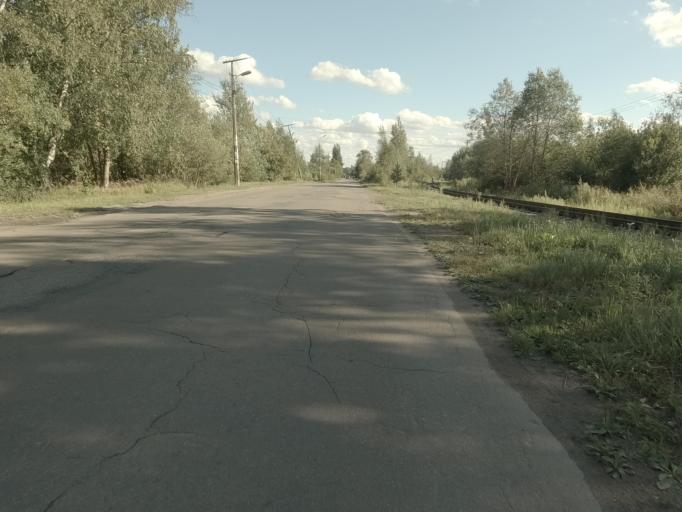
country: RU
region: Leningrad
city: Imeni Morozova
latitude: 59.9664
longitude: 31.0288
